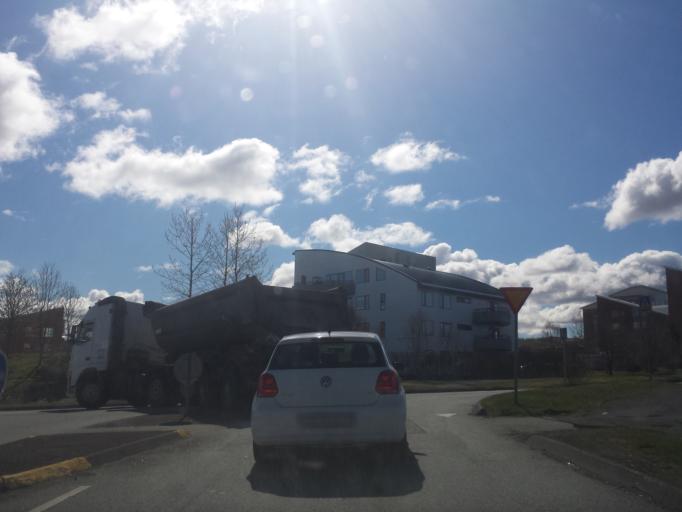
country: IS
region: Capital Region
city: Kopavogur
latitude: 64.0987
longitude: -21.8748
